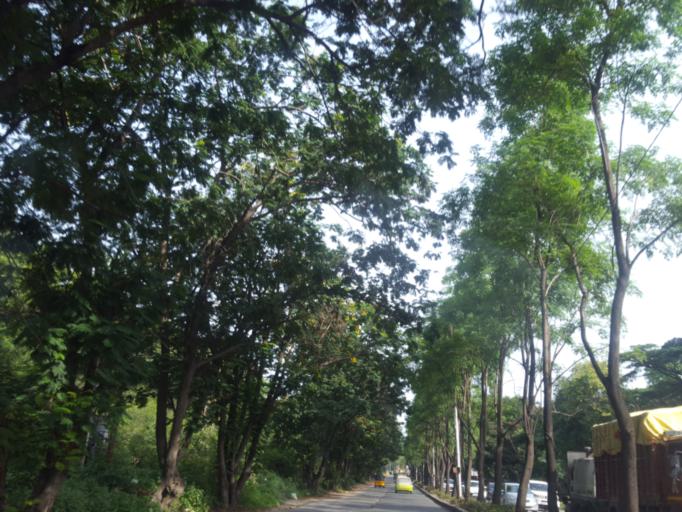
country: IN
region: Telangana
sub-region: Medak
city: Serilingampalle
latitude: 17.4581
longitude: 78.3388
